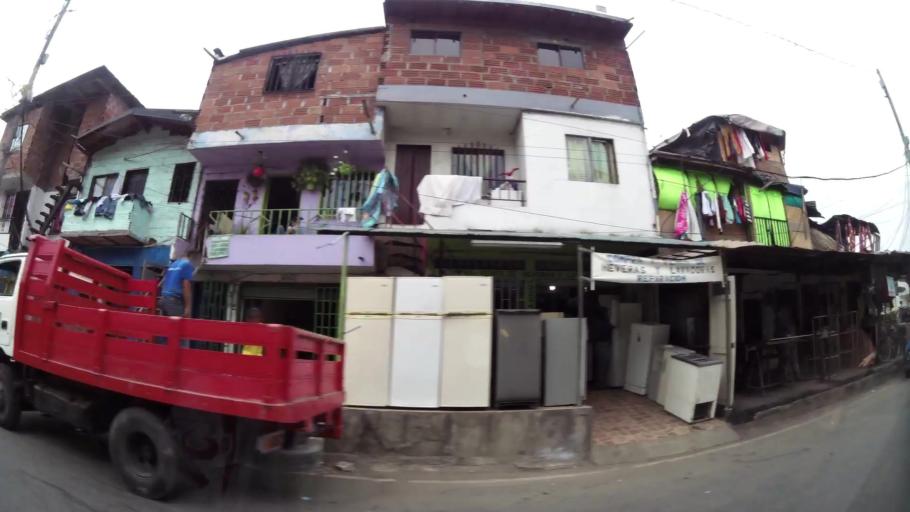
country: CO
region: Antioquia
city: Medellin
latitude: 6.2827
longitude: -75.5660
